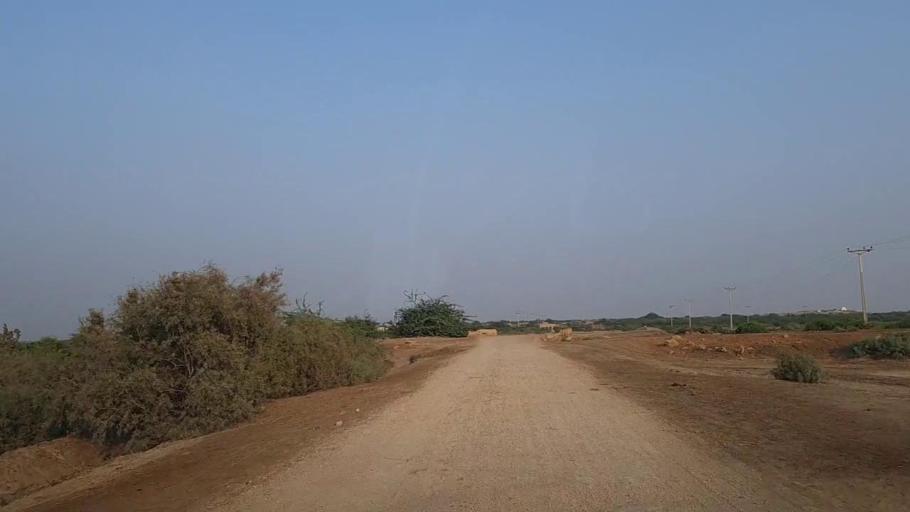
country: PK
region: Sindh
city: Thatta
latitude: 24.6904
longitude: 67.8127
